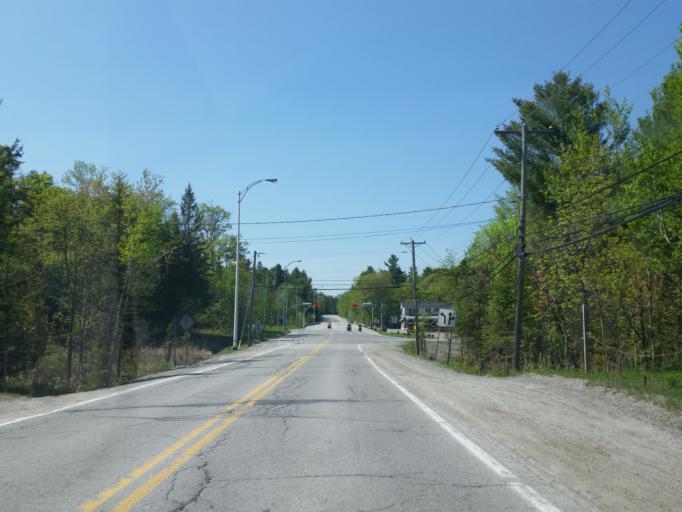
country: CA
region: Quebec
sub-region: Outaouais
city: Wakefield
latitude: 45.5730
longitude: -75.8696
